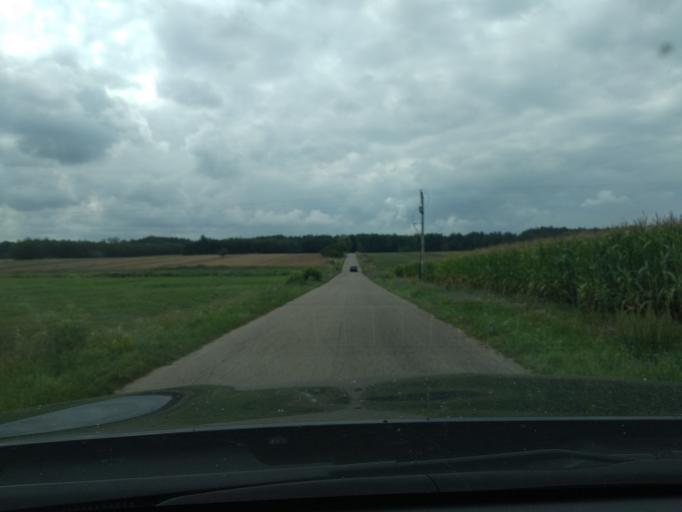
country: PL
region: Masovian Voivodeship
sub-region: Powiat pultuski
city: Obryte
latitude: 52.7126
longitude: 21.1904
